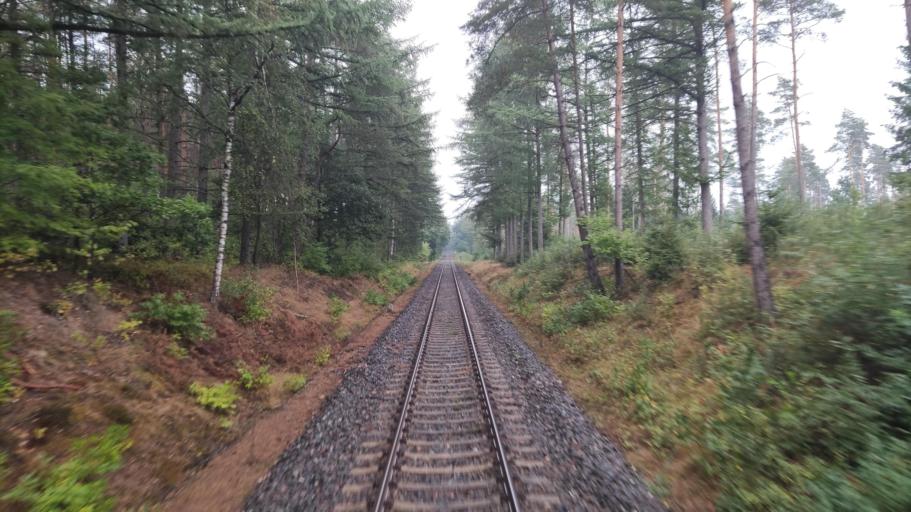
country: DE
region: Lower Saxony
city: Bispingen
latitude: 53.0698
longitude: 9.9822
